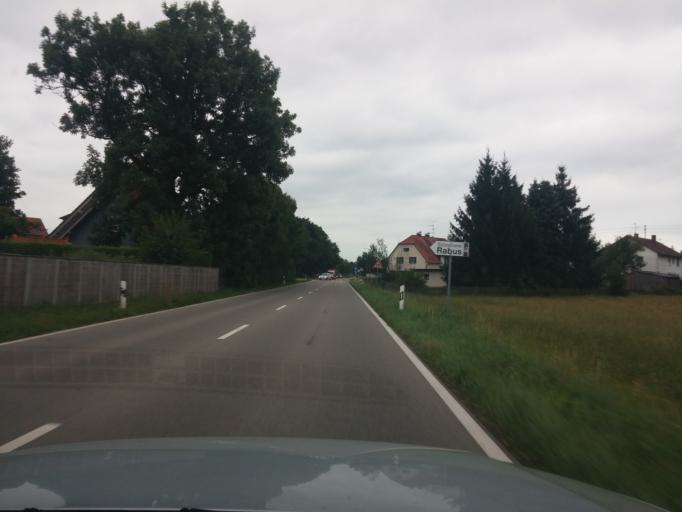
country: DE
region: Baden-Wuerttemberg
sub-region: Tuebingen Region
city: Aitrach
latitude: 47.9550
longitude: 10.1141
